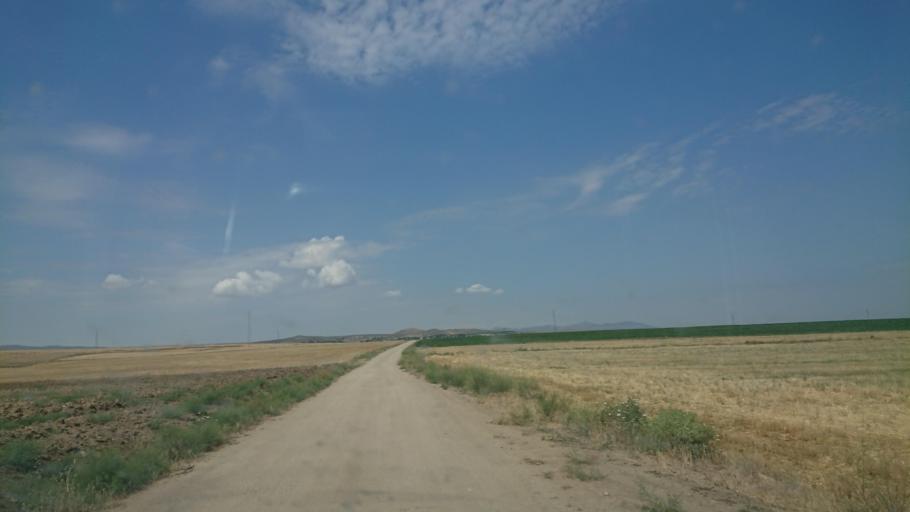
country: TR
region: Aksaray
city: Agacoren
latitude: 38.9560
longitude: 33.9186
